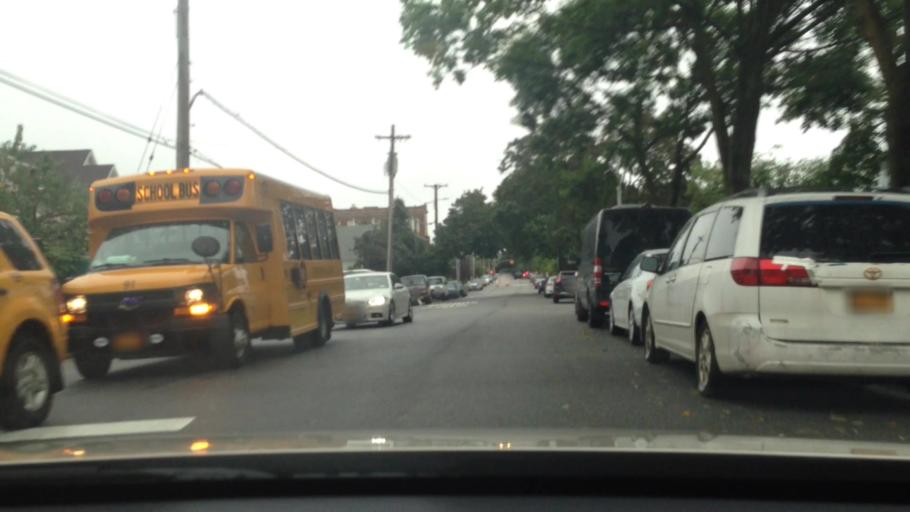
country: US
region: New York
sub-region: Nassau County
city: Bellerose
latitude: 40.7314
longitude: -73.7204
